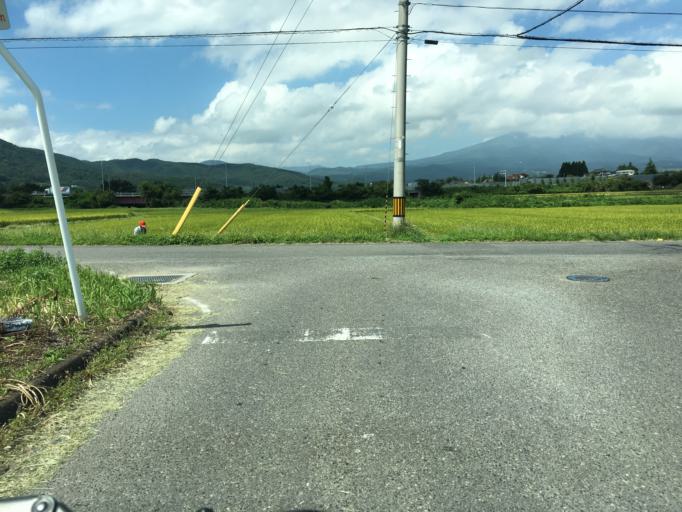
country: JP
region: Fukushima
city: Motomiya
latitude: 37.5175
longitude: 140.3846
